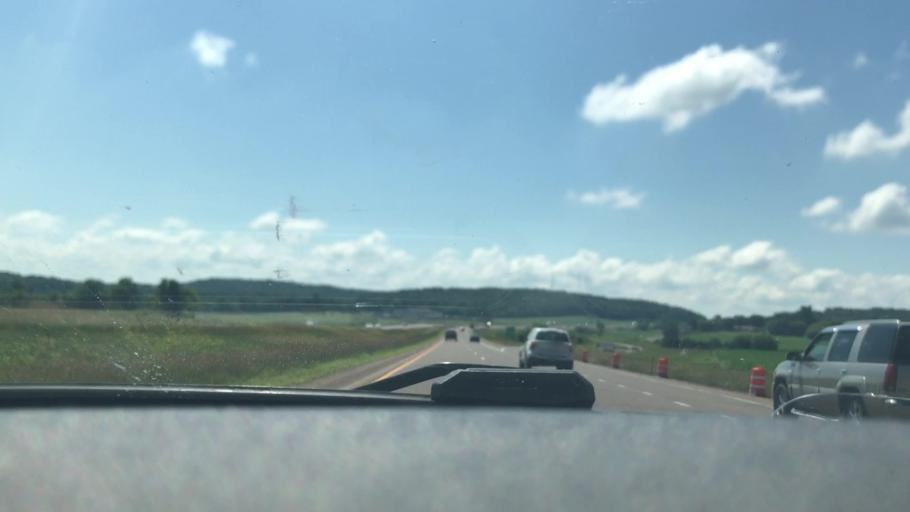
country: US
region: Wisconsin
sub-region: Chippewa County
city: Chippewa Falls
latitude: 44.9704
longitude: -91.4308
